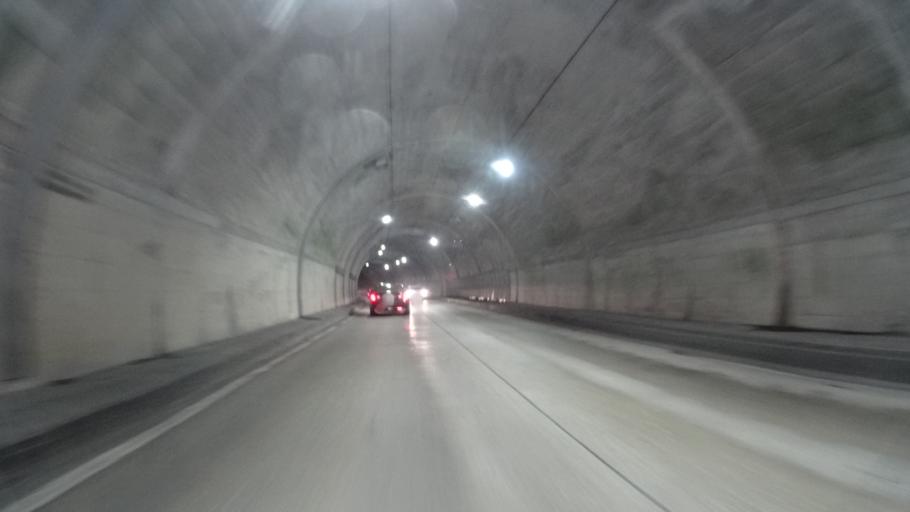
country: JP
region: Ishikawa
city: Tsurugi-asahimachi
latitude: 36.3733
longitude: 136.5713
